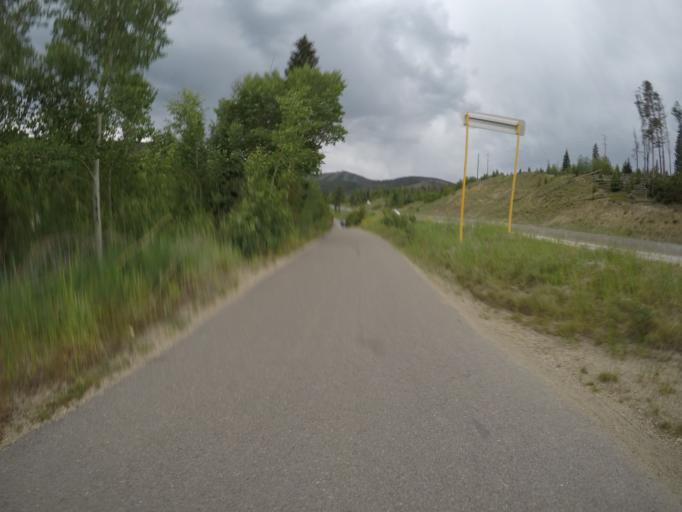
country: US
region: Colorado
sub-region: Grand County
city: Fraser
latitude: 39.9117
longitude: -105.7819
